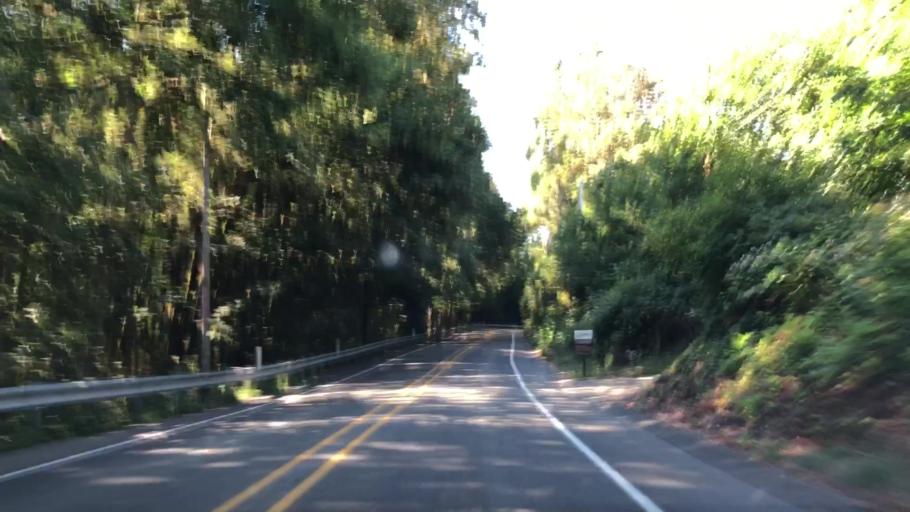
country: US
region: Washington
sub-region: Kitsap County
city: Kingston
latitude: 47.7792
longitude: -122.4996
